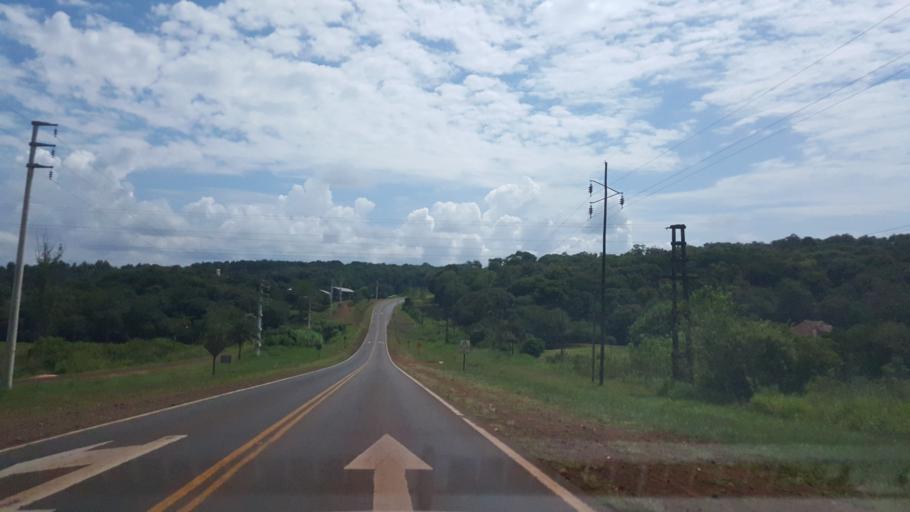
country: AR
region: Misiones
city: Capiovi
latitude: -26.8632
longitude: -55.0452
